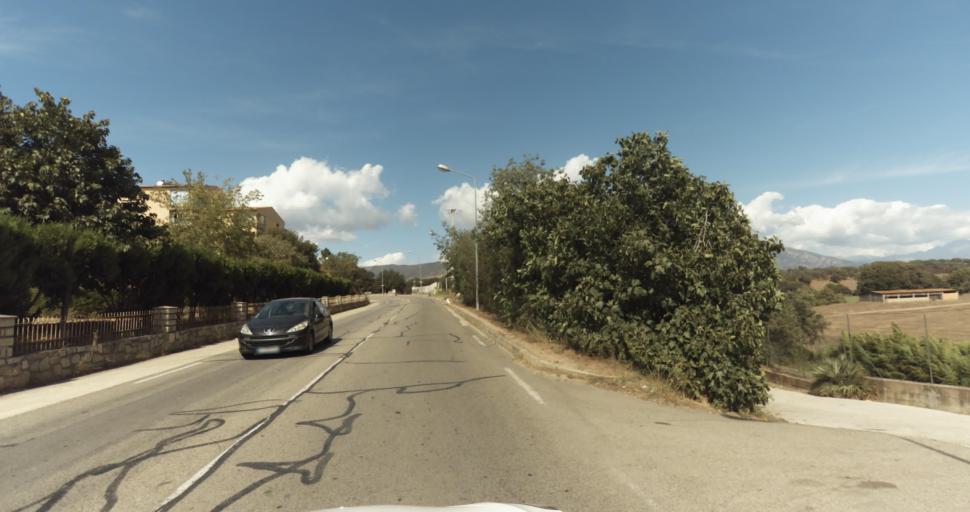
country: FR
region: Corsica
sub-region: Departement de la Corse-du-Sud
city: Afa
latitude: 41.9543
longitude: 8.7840
